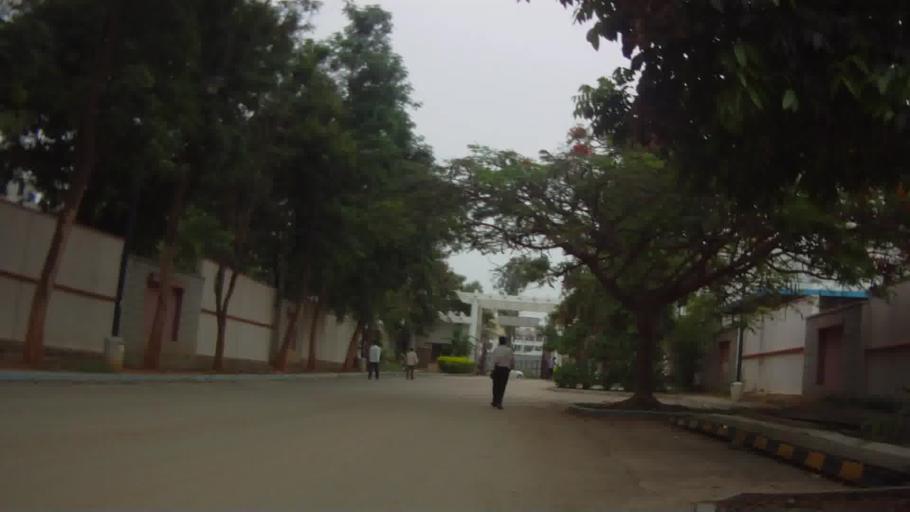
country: IN
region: Karnataka
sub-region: Bangalore Rural
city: Hoskote
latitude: 12.9623
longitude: 77.7505
